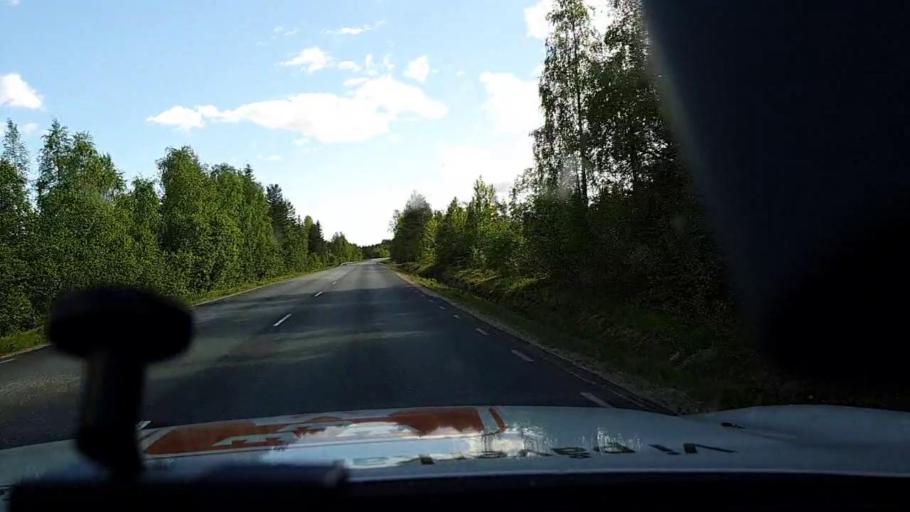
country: FI
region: Lapland
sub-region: Torniolaakso
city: Ylitornio
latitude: 66.3401
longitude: 23.6460
